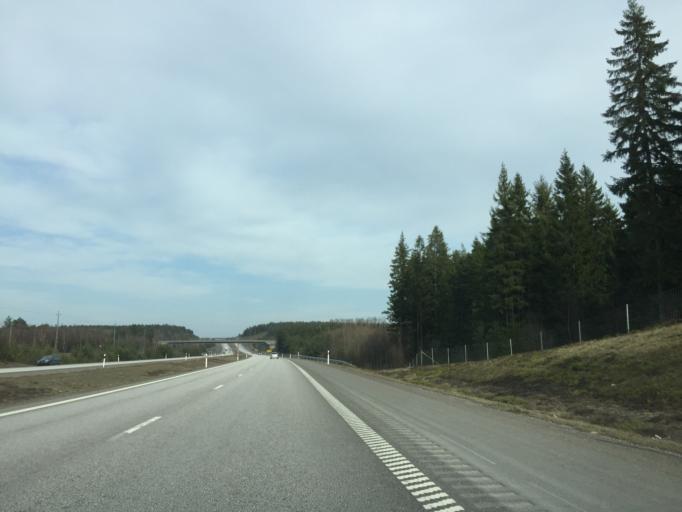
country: SE
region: OErebro
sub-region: Lindesbergs Kommun
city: Fellingsbro
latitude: 59.3790
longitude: 15.6472
